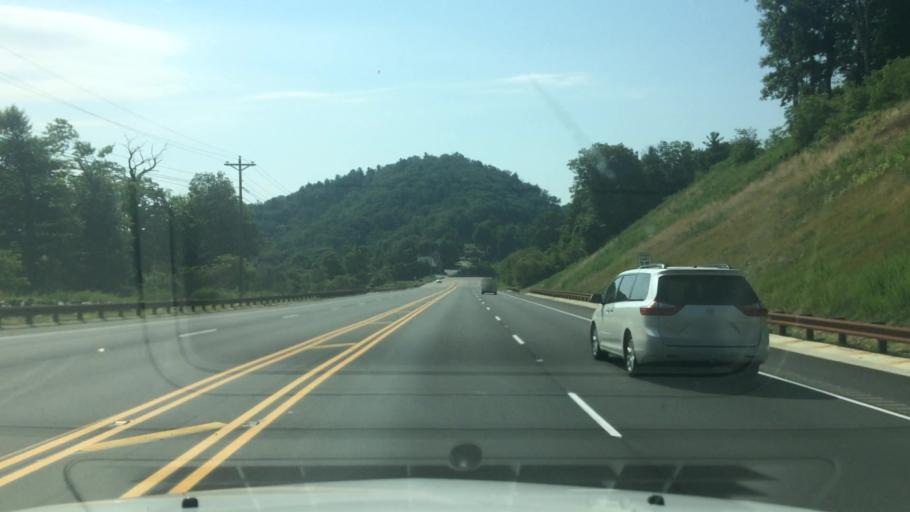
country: US
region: North Carolina
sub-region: Watauga County
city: Blowing Rock
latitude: 36.1071
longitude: -81.6501
